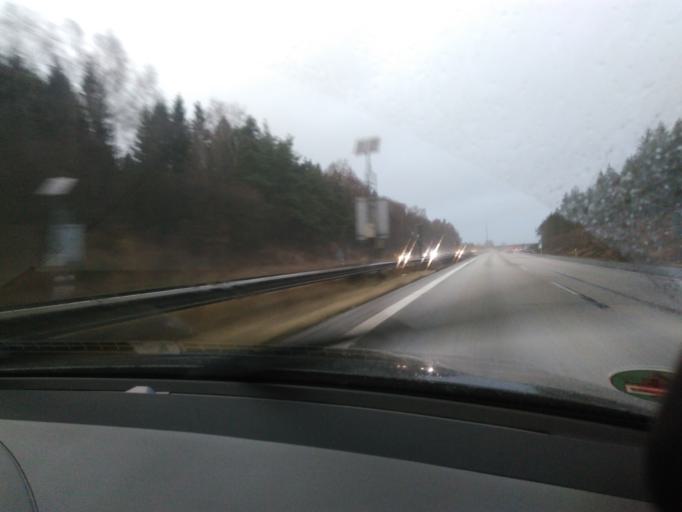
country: DE
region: Schleswig-Holstein
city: Schmalfeld
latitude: 53.8985
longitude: 9.9386
